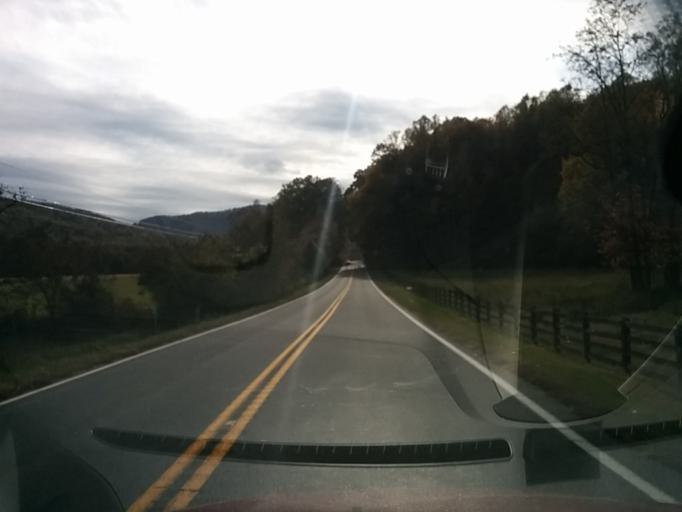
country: US
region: Virginia
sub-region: Nelson County
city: Nellysford
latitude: 37.8762
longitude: -78.9108
